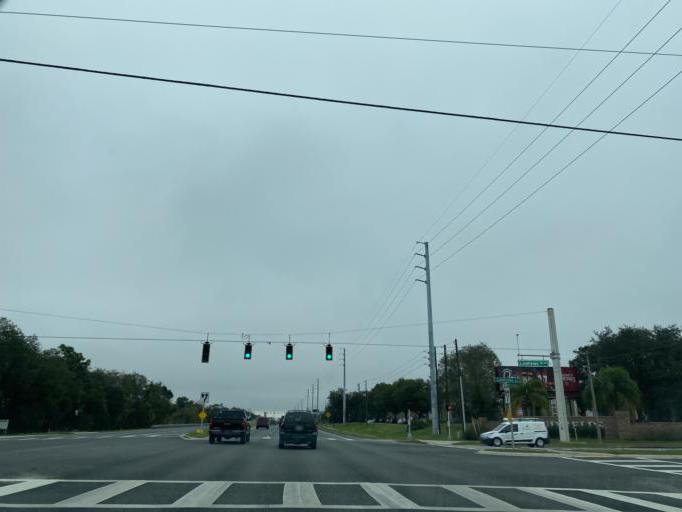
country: US
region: Florida
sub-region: Polk County
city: Citrus Ridge
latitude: 28.3468
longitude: -81.6390
